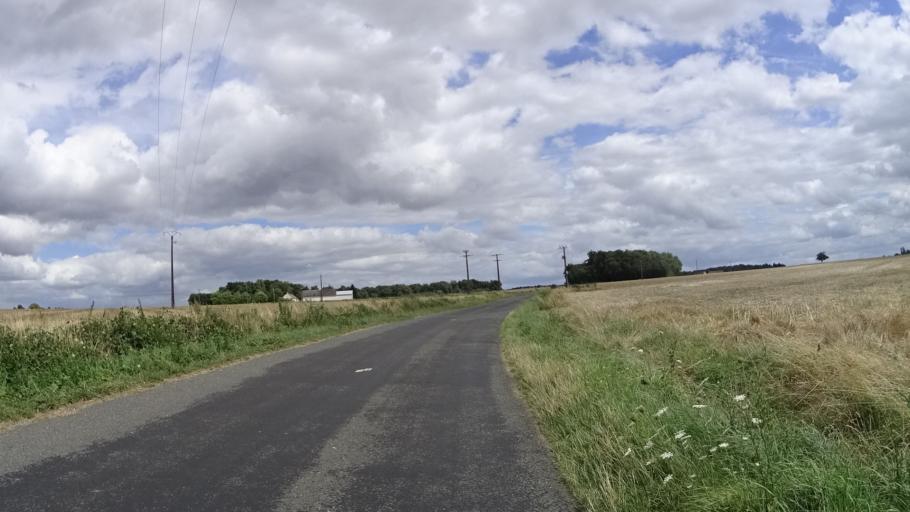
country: FR
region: Centre
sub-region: Departement du Loiret
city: Douchy
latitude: 47.9730
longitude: 3.0856
